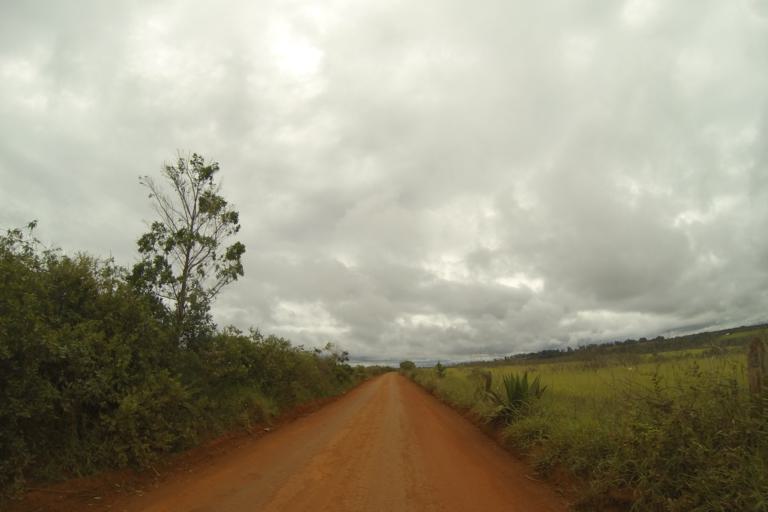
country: BR
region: Minas Gerais
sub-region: Campos Altos
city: Campos Altos
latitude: -19.8785
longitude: -46.2998
